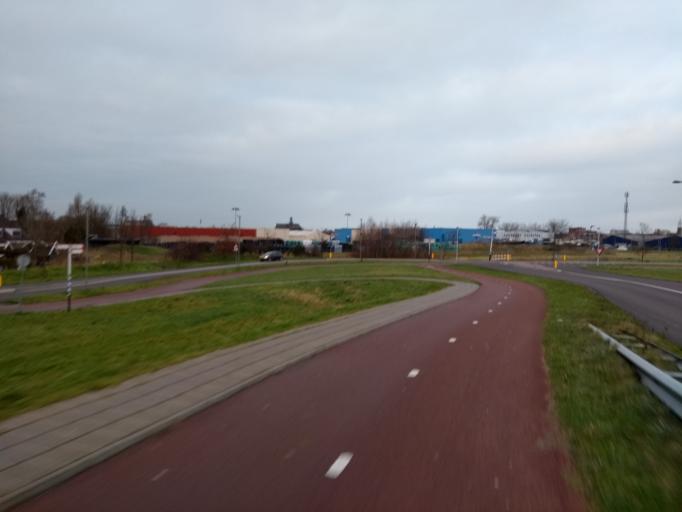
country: NL
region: Friesland
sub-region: Sudwest Fryslan
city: Sneek
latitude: 53.0228
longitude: 5.6626
